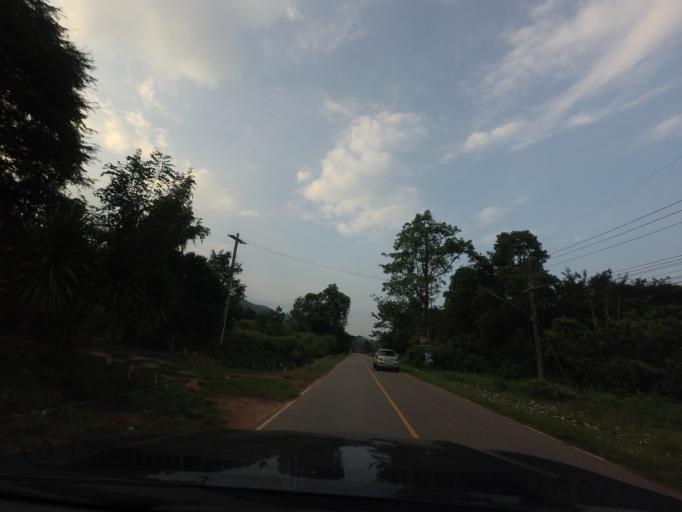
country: TH
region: Loei
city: Na Haeo
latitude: 17.4017
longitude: 101.0469
